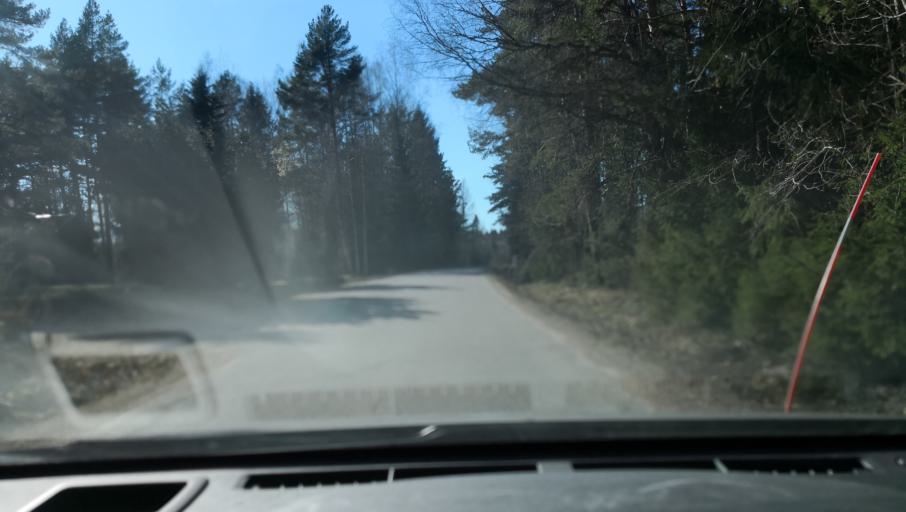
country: SE
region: Dalarna
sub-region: Avesta Kommun
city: Horndal
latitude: 60.0825
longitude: 16.4428
